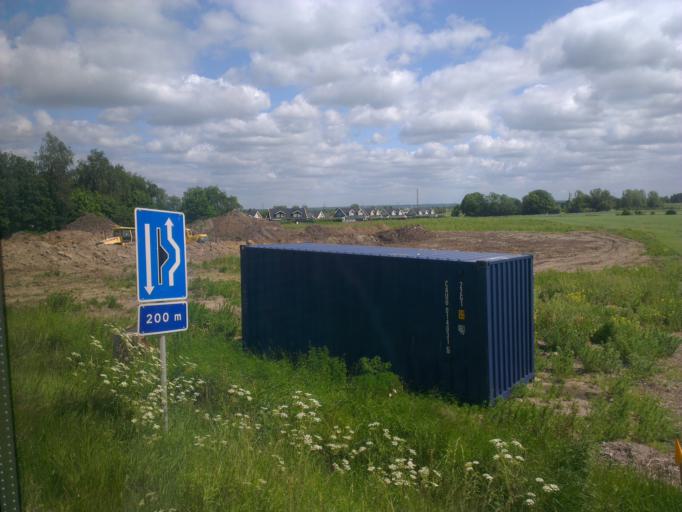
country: DK
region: Capital Region
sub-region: Frederikssund Kommune
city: Slangerup
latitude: 55.8799
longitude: 12.1937
